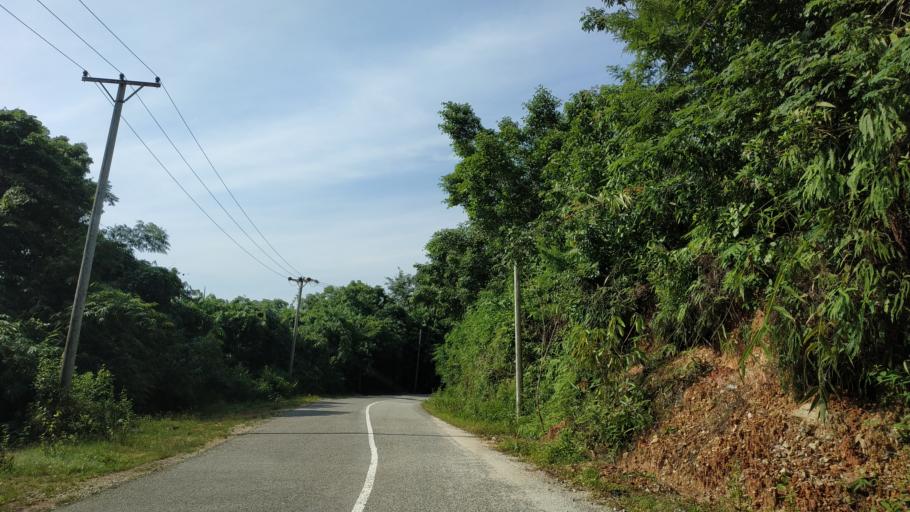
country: TH
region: Kanchanaburi
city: Thong Pha Phum
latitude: 14.6249
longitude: 98.1138
